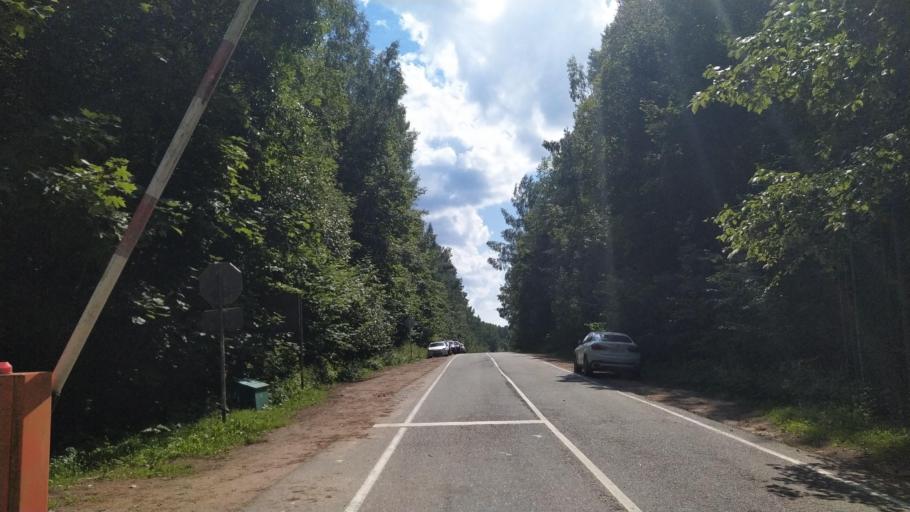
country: RU
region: Pskov
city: Pushkinskiye Gory
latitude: 57.0747
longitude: 28.9564
